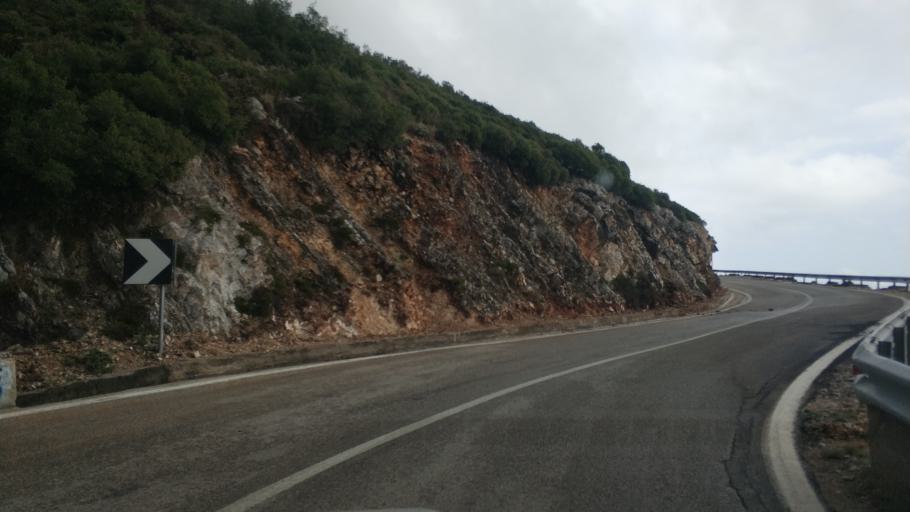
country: AL
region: Vlore
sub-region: Rrethi i Vlores
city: Vranisht
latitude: 40.1853
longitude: 19.5947
